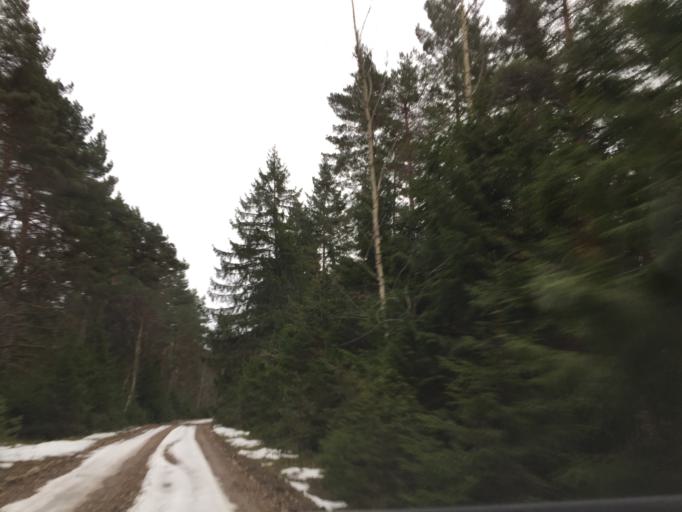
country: EE
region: Saare
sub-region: Kuressaare linn
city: Kuressaare
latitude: 58.4822
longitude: 22.2469
